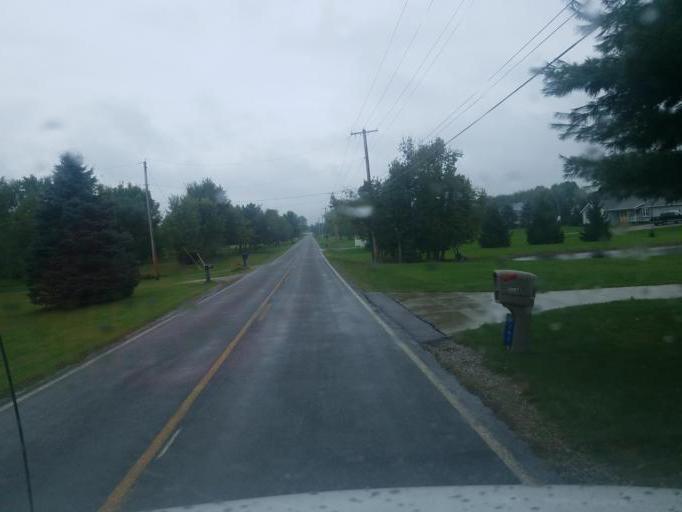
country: US
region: Ohio
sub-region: Medina County
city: Seville
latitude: 41.0203
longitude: -81.8150
